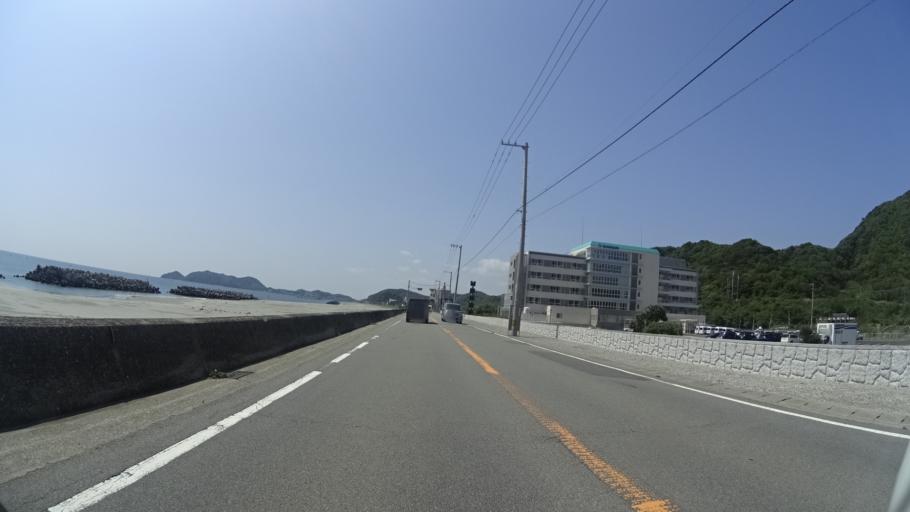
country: JP
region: Tokushima
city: Narutocho-mitsuishi
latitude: 34.2064
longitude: 134.6265
